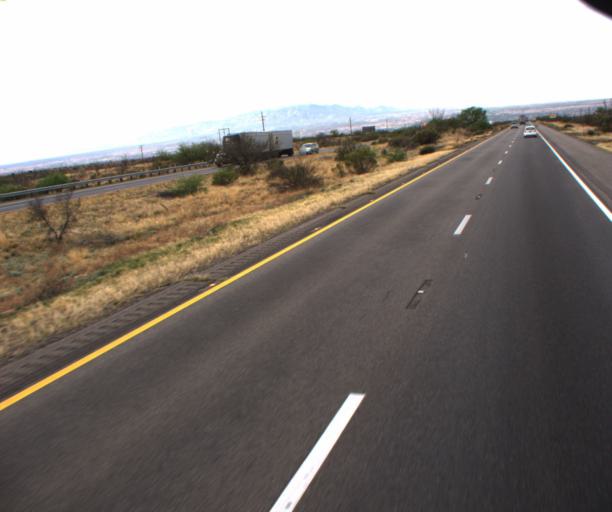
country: US
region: Arizona
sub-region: Cochise County
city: Saint David
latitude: 31.9851
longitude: -110.1986
